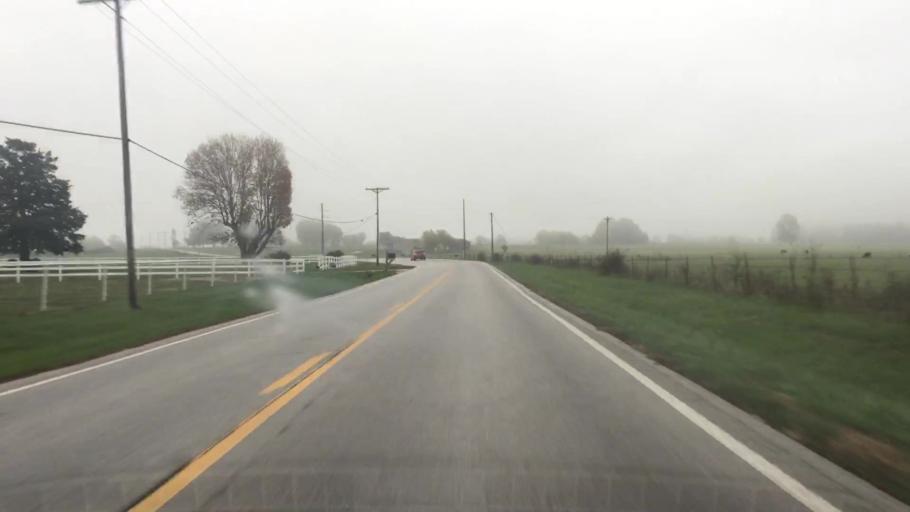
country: US
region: Missouri
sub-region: Callaway County
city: Fulton
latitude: 38.8745
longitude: -92.0675
